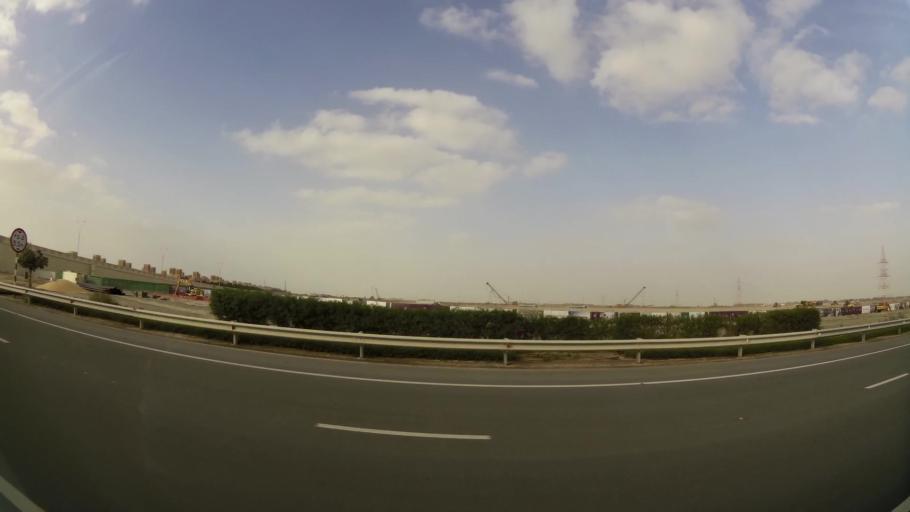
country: AE
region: Abu Dhabi
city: Abu Dhabi
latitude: 24.4974
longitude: 54.6038
